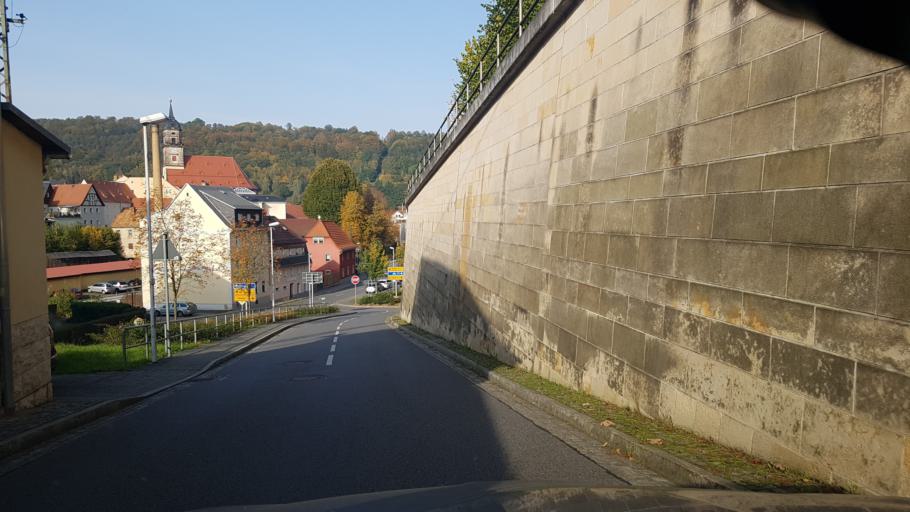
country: DE
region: Saxony
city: Konigstein
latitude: 50.9155
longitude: 14.0721
